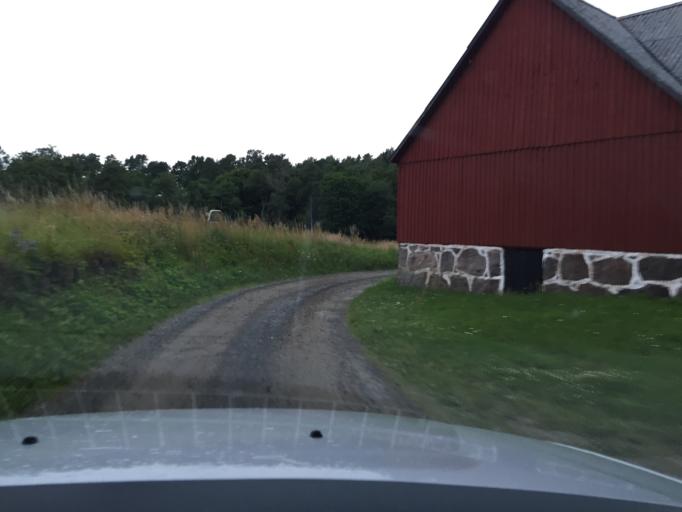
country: SE
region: Skane
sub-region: Kristianstads Kommun
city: Degeberga
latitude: 55.7271
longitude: 14.1257
